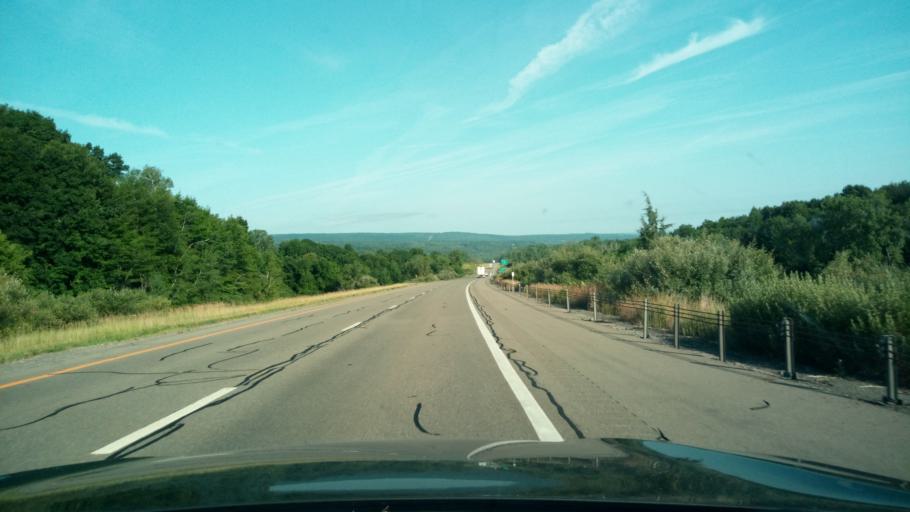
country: US
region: New York
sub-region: Livingston County
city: Dansville
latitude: 42.5352
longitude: -77.6788
